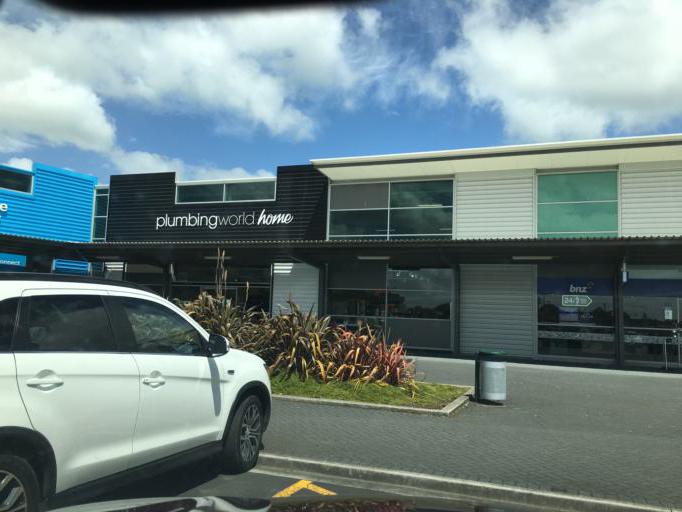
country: NZ
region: Waikato
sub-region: Waipa District
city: Cambridge
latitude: -38.0079
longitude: 175.3407
